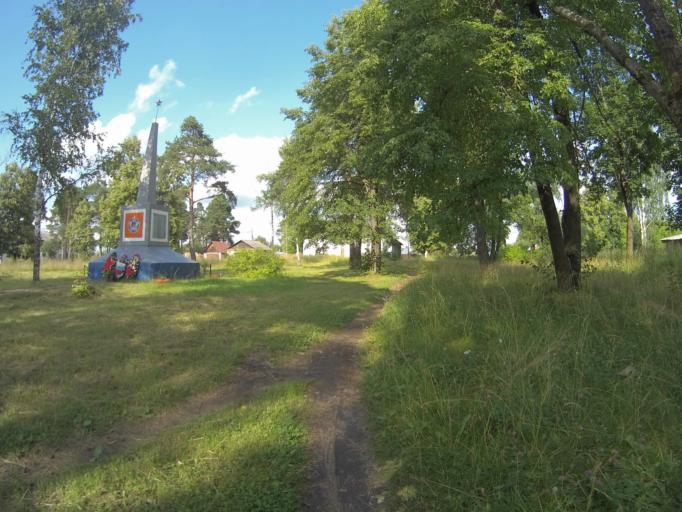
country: RU
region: Vladimir
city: Orgtrud
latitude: 56.2867
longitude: 40.7799
